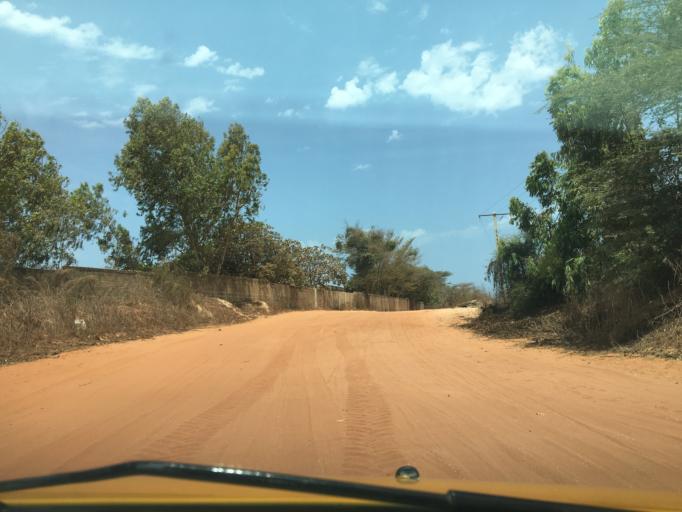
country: SN
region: Thies
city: Thies
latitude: 14.8176
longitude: -17.1980
